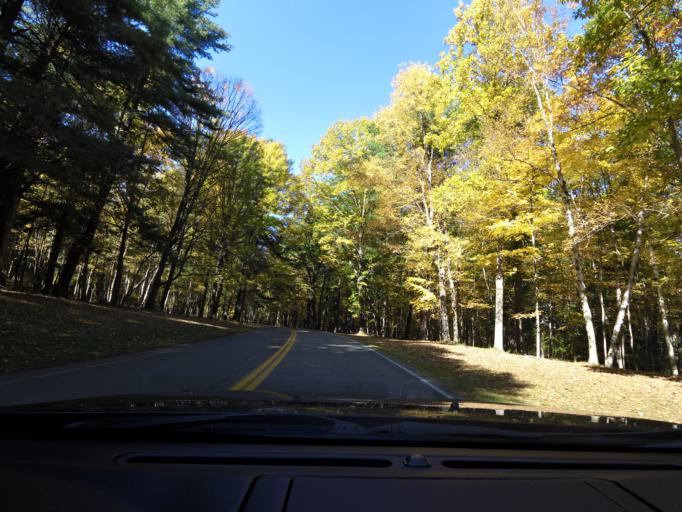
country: US
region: New York
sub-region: Wyoming County
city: Castile
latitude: 42.5950
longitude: -78.0143
